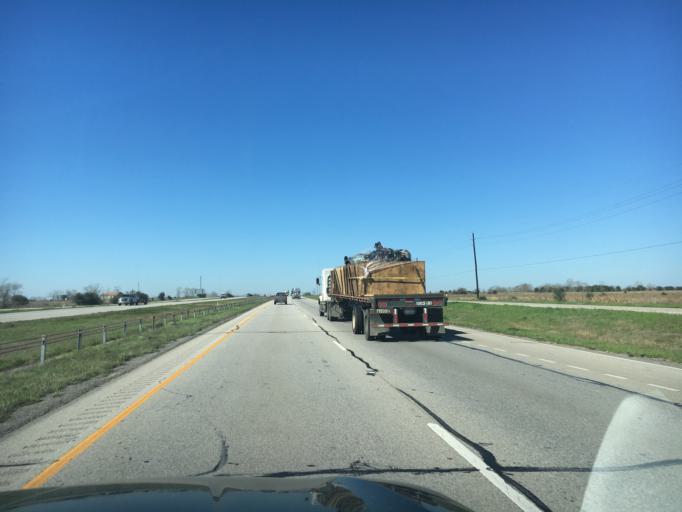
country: US
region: Texas
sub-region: Austin County
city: Sealy
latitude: 29.7576
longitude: -96.2281
